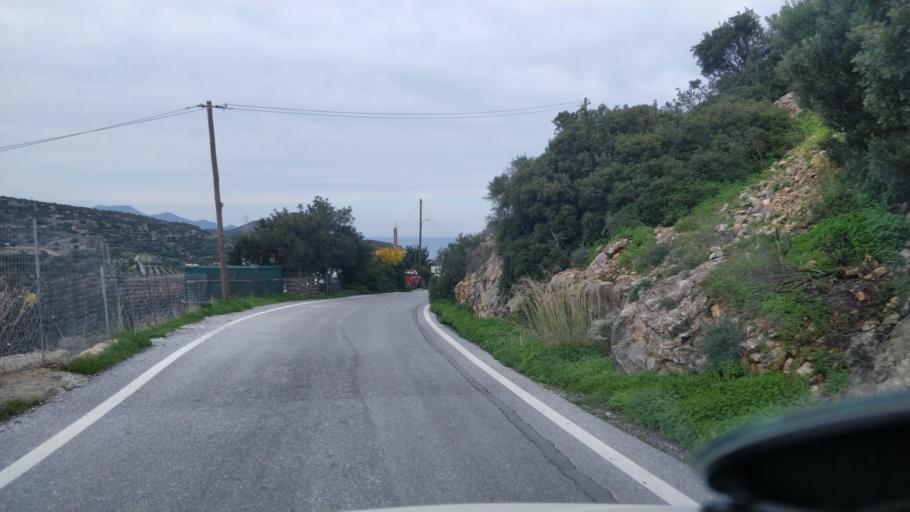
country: GR
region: Crete
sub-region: Nomos Lasithiou
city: Agios Nikolaos
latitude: 35.1133
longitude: 25.7215
